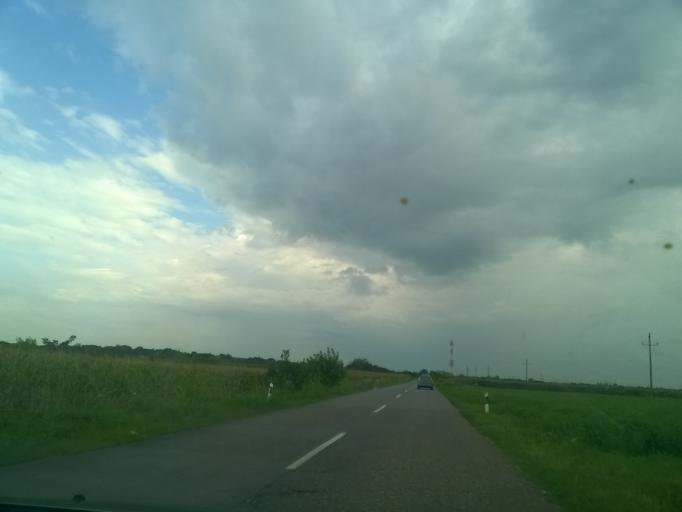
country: RS
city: Tomasevac
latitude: 45.2559
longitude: 20.6291
